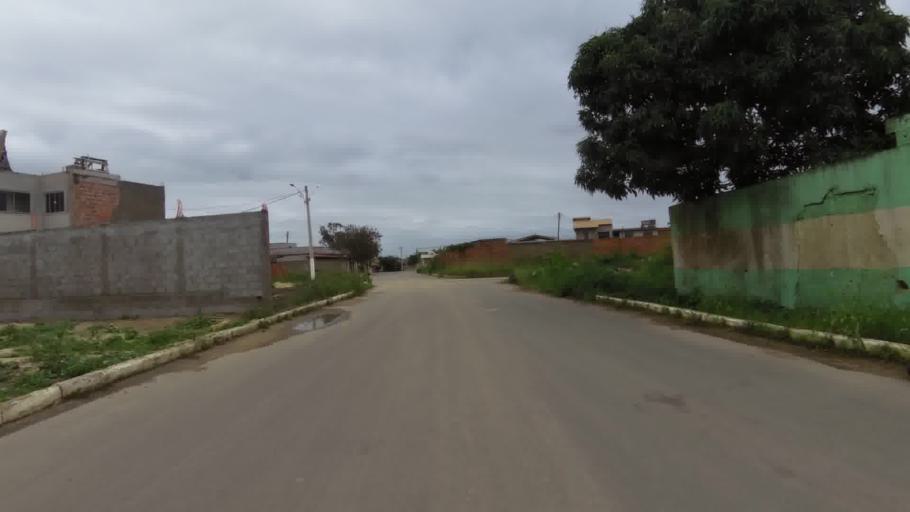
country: BR
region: Espirito Santo
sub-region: Marataizes
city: Marataizes
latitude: -21.0467
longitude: -40.8389
